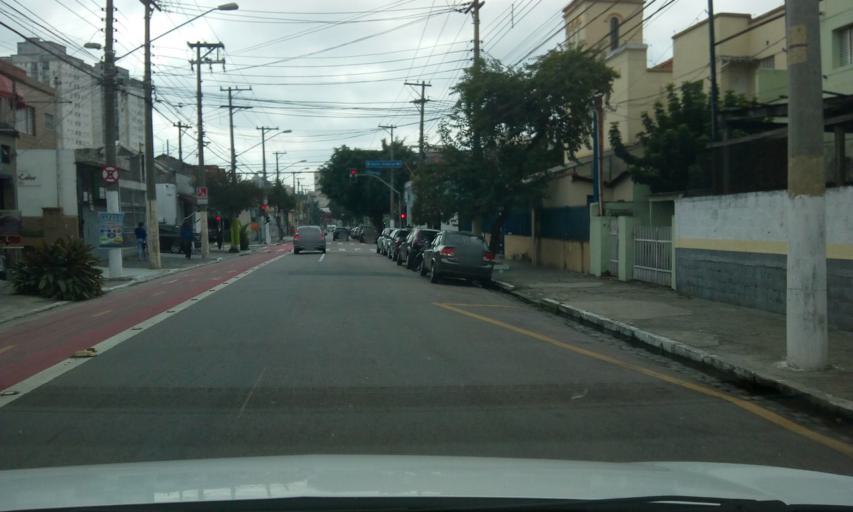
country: BR
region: Sao Paulo
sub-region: Sao Paulo
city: Sao Paulo
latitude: -23.5480
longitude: -46.5943
